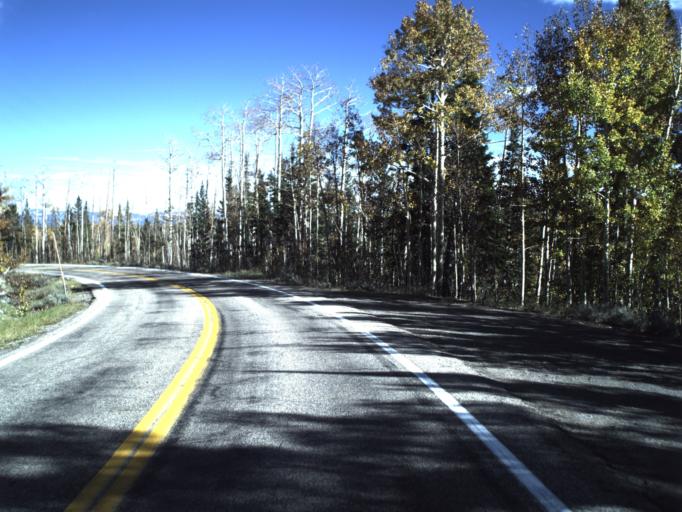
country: US
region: Utah
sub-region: Iron County
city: Parowan
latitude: 37.6543
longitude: -112.7579
